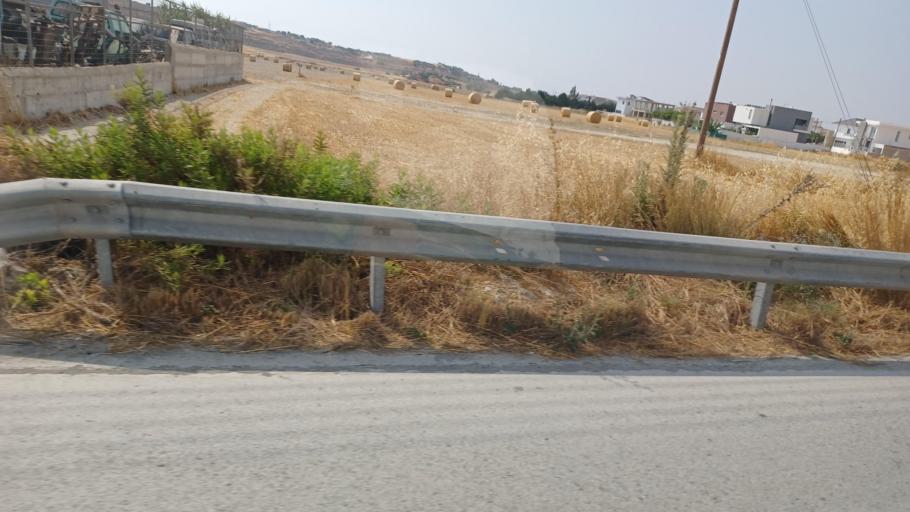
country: CY
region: Larnaka
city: Aradippou
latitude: 34.9318
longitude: 33.5437
